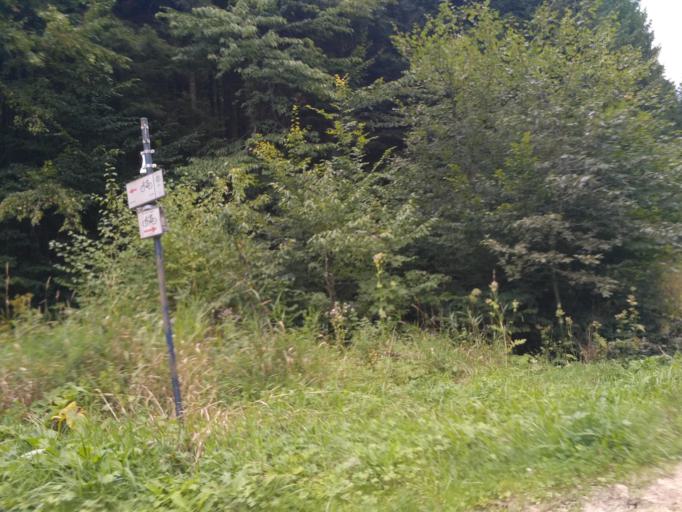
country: PL
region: Subcarpathian Voivodeship
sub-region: Powiat rzeszowski
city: Dynow
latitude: 49.7558
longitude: 22.2910
